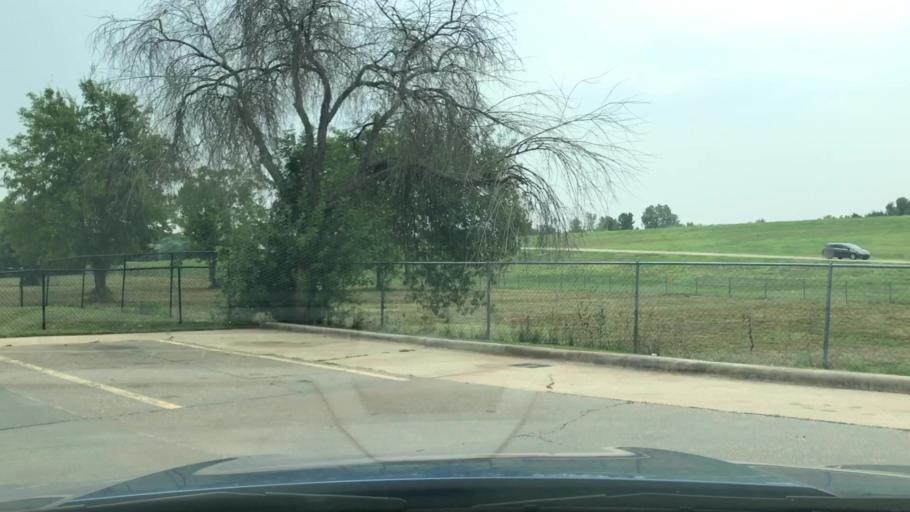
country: US
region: Louisiana
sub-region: Bossier Parish
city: Bossier City
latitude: 32.4127
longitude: -93.7235
